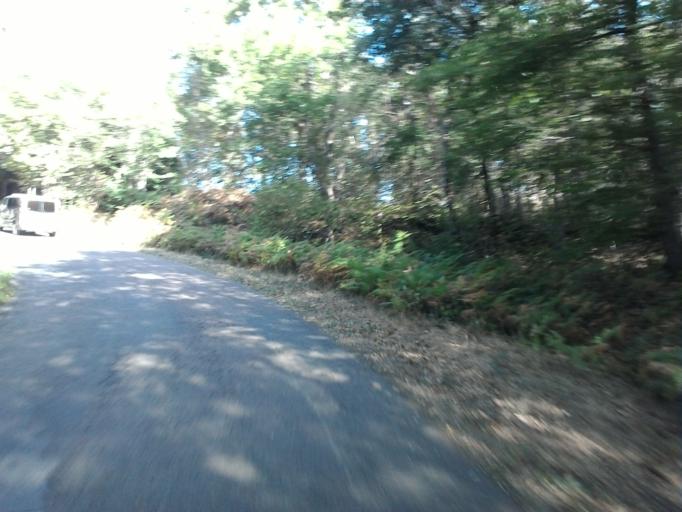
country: FR
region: Bourgogne
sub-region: Departement de la Nievre
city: Lormes
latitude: 47.3056
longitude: 3.8932
